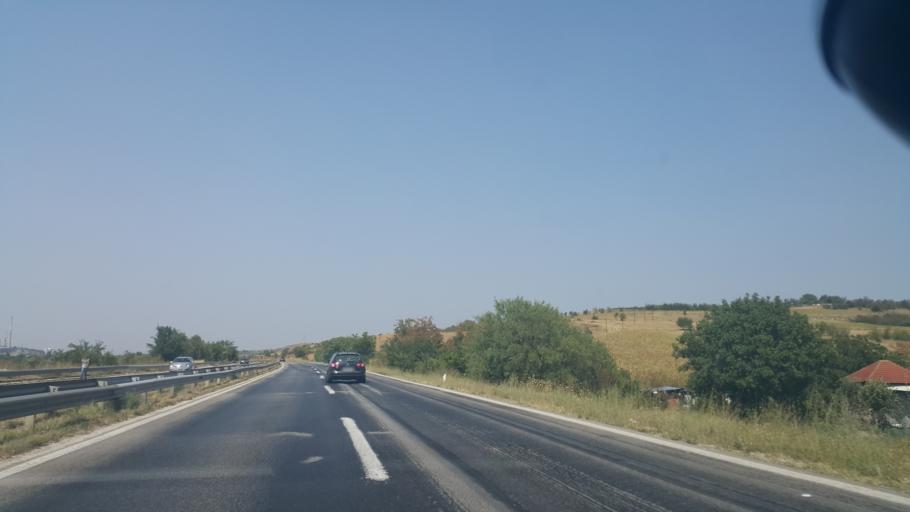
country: MK
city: Miladinovci
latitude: 41.9726
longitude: 21.6481
